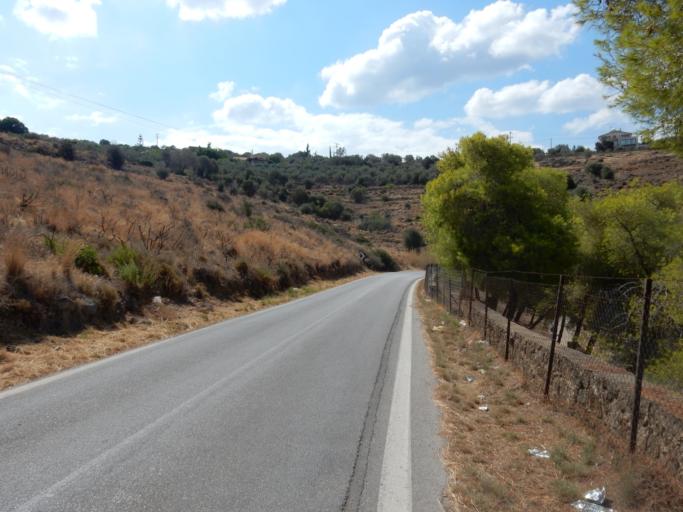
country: GR
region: Attica
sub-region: Nomos Piraios
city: Aegina
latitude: 37.6949
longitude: 23.4662
